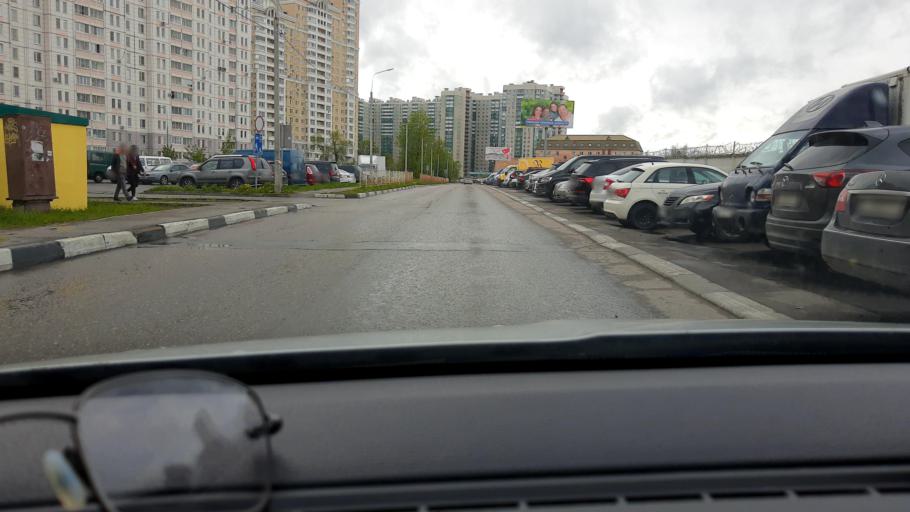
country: RU
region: Moskovskaya
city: Opalikha
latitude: 55.8331
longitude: 37.2893
